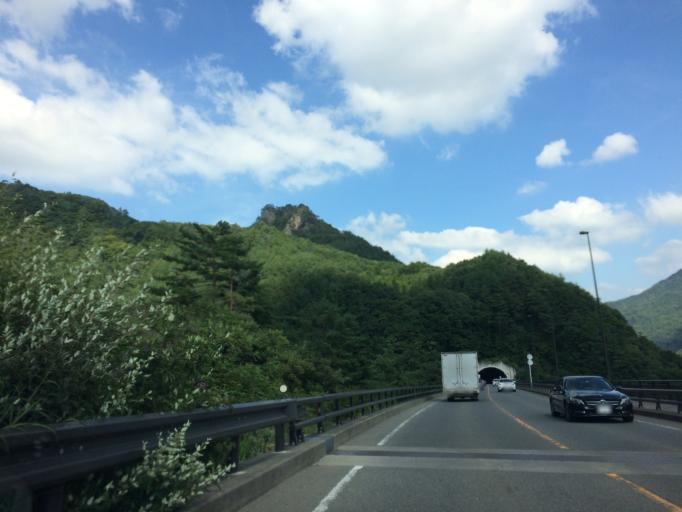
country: JP
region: Gunma
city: Nakanojomachi
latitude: 36.5499
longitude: 138.6868
